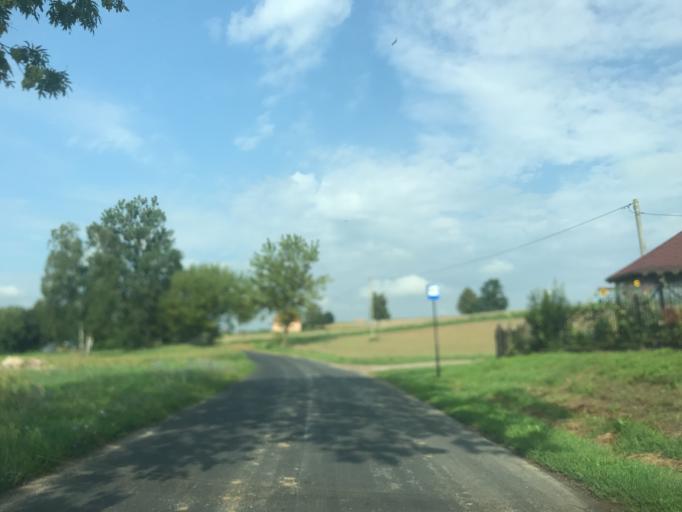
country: PL
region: Warmian-Masurian Voivodeship
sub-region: Powiat nowomiejski
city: Kurzetnik
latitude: 53.3689
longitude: 19.5780
